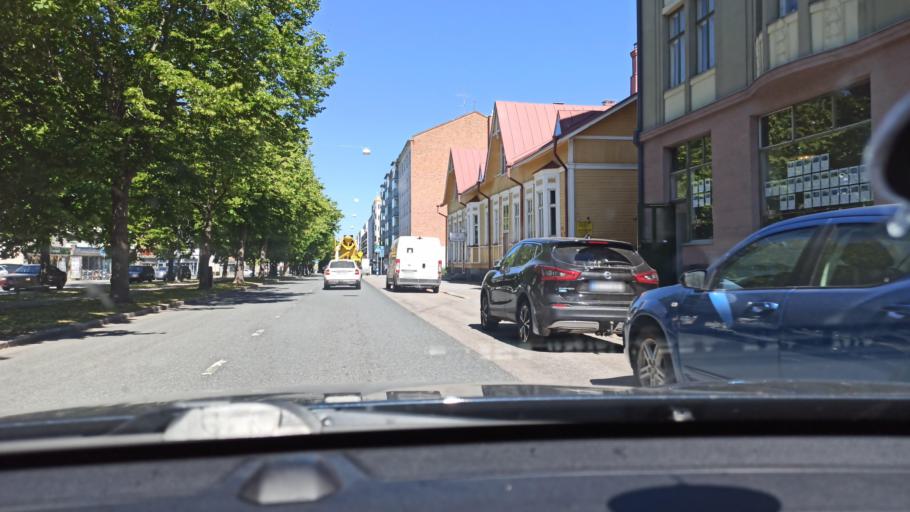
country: FI
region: Ostrobothnia
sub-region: Vaasa
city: Vaasa
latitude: 63.0910
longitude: 21.6204
